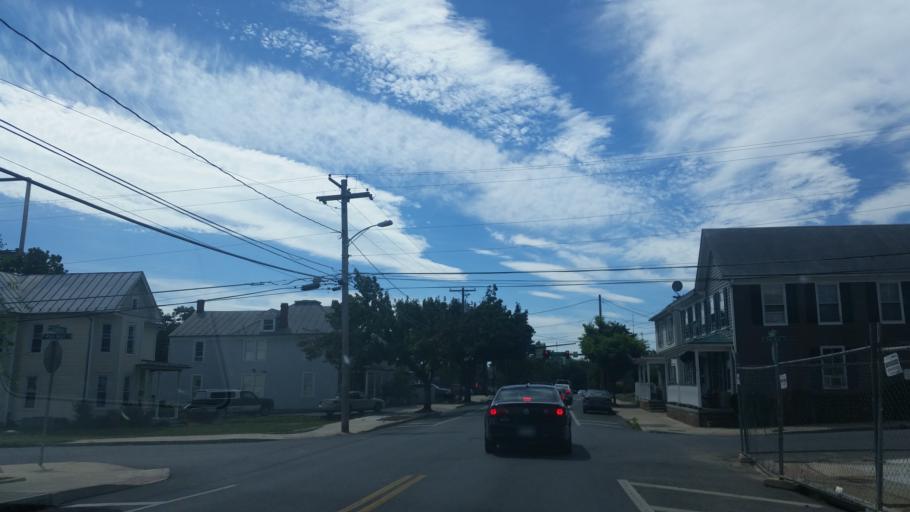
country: US
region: Virginia
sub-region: City of Winchester
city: Winchester
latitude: 39.1783
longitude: -78.1696
